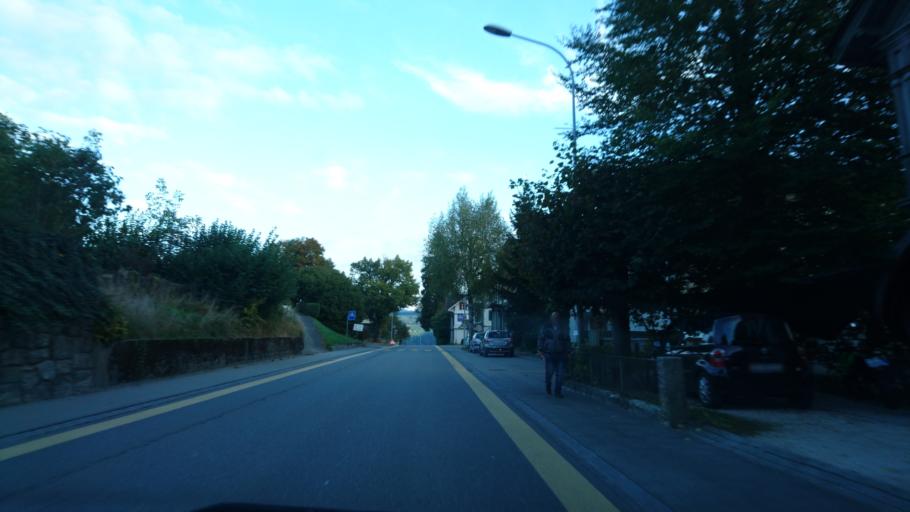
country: CH
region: Bern
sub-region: Bern-Mittelland District
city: Zaziwil
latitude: 46.9050
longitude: 7.6429
